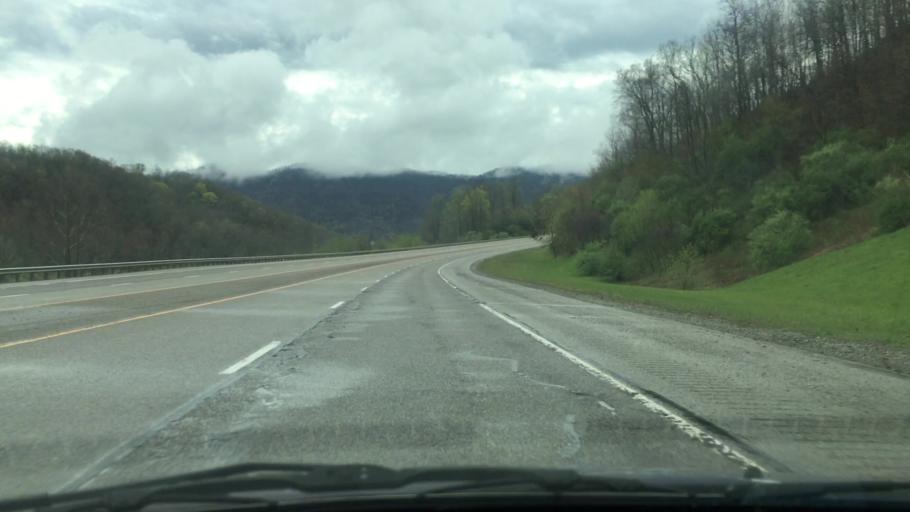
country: US
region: Kentucky
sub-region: Letcher County
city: Jenkins
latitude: 37.2033
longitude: -82.6229
